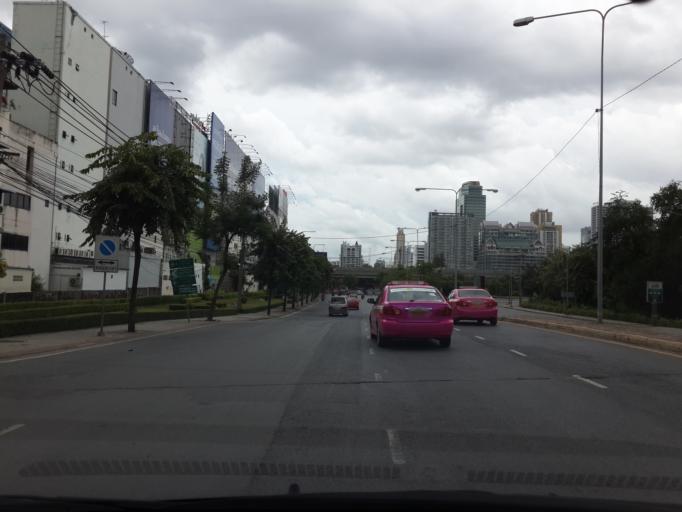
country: TH
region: Bangkok
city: Din Daeng
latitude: 13.7546
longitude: 100.5700
